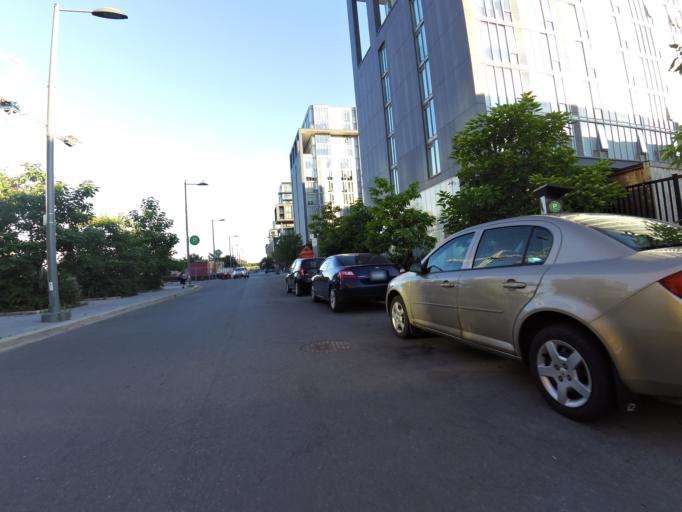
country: CA
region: Ontario
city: Toronto
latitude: 43.6541
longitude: -79.3563
